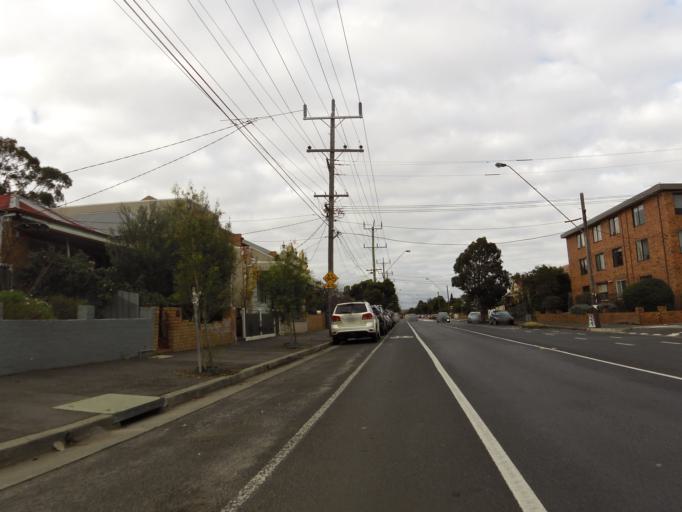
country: AU
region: Victoria
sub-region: Moreland
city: Brunswick
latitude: -37.7720
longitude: 144.9666
